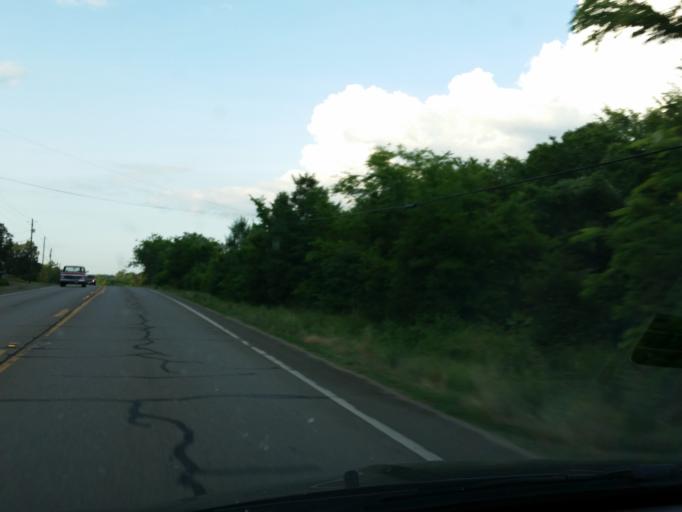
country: US
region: Georgia
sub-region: Walker County
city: Chattanooga Valley
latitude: 34.9437
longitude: -85.4465
